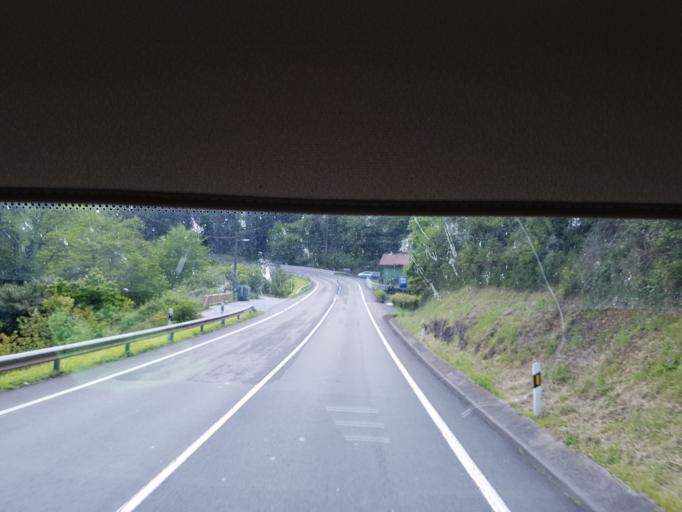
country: ES
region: Basque Country
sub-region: Bizkaia
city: San Julian de Muskiz
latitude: 43.2996
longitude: -3.1250
